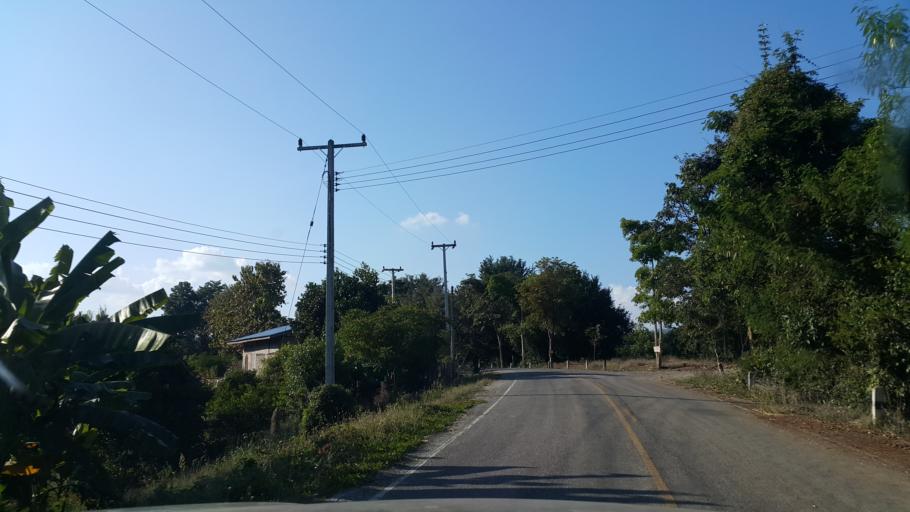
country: TH
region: Sukhothai
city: Thung Saliam
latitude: 17.3876
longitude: 99.5177
